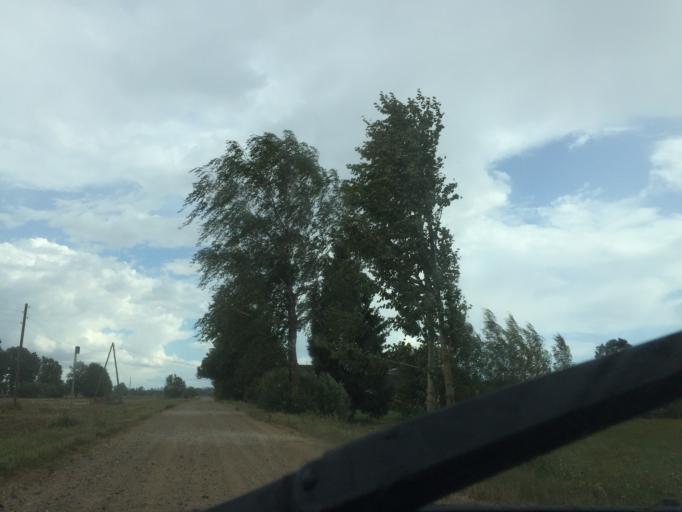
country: LT
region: Siauliu apskritis
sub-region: Joniskis
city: Joniskis
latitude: 56.3558
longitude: 23.5284
